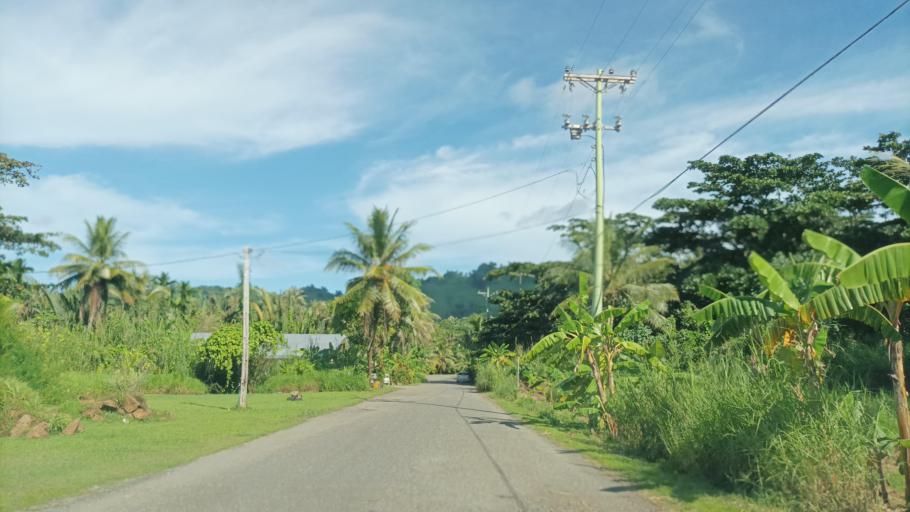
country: FM
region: Kosrae
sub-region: Lelu Municipality
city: Tofol
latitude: 5.3197
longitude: 163.0165
